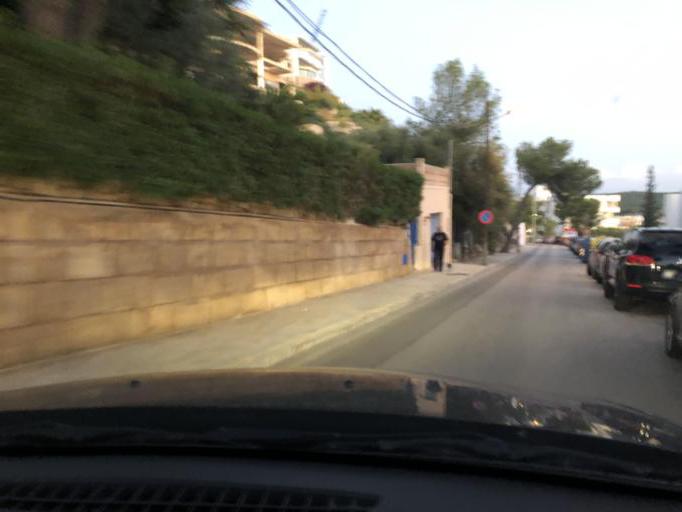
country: ES
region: Balearic Islands
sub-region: Illes Balears
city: Santa Ponsa
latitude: 39.5210
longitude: 2.4761
